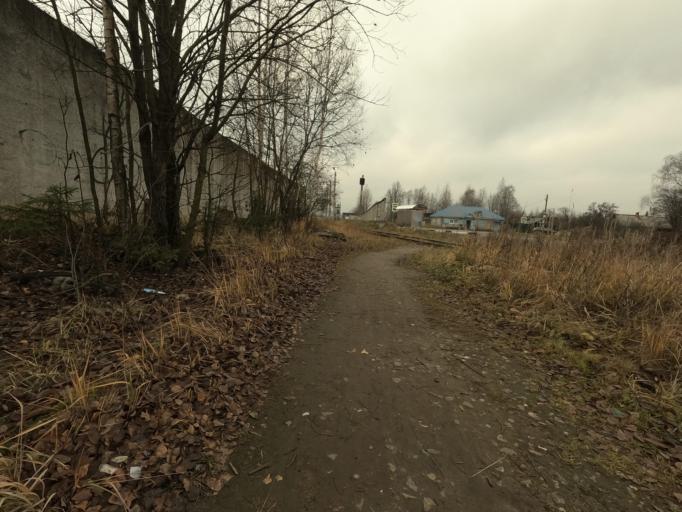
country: RU
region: Leningrad
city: Lyuban'
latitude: 59.4935
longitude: 31.2737
